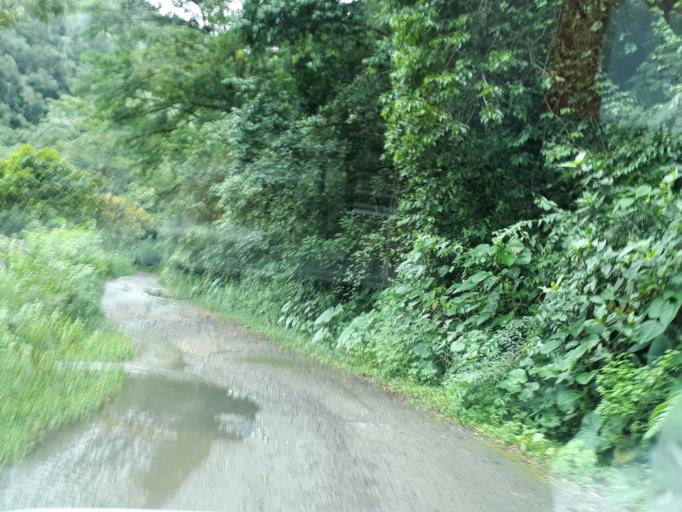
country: CO
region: Boyaca
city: Santa Maria
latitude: 4.7381
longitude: -73.3105
